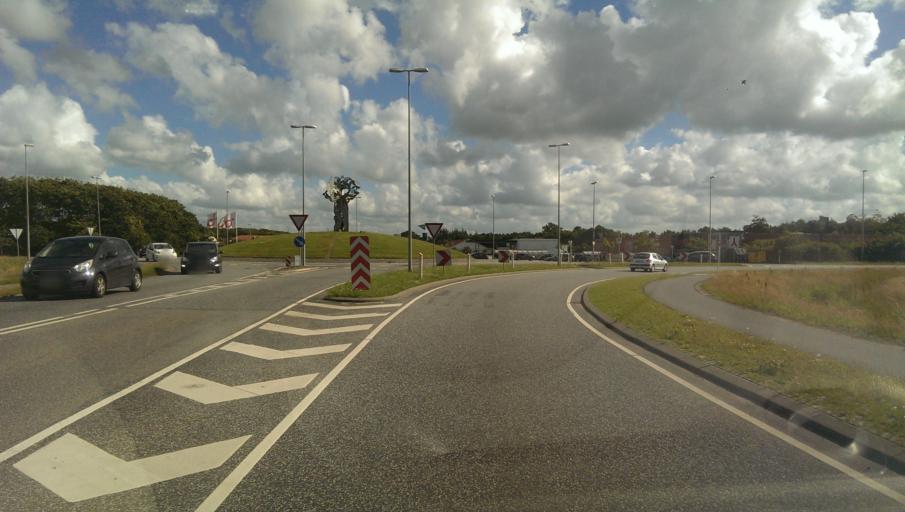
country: DK
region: Central Jutland
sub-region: Ringkobing-Skjern Kommune
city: Tarm
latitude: 55.9195
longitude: 8.5169
